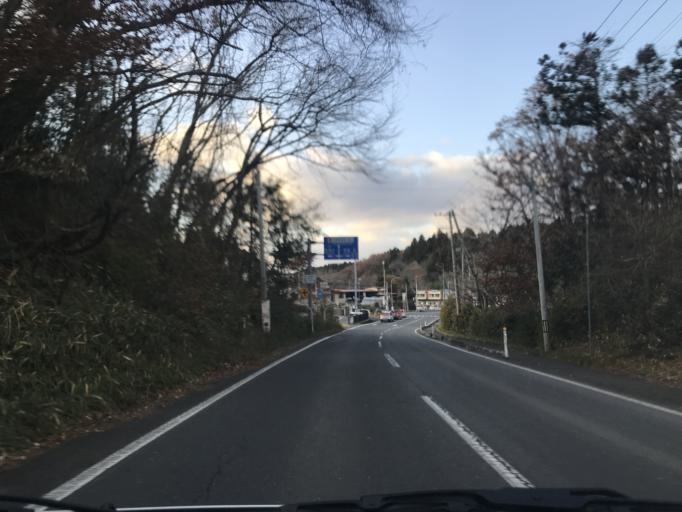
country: JP
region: Miyagi
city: Kogota
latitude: 38.6529
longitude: 141.0721
